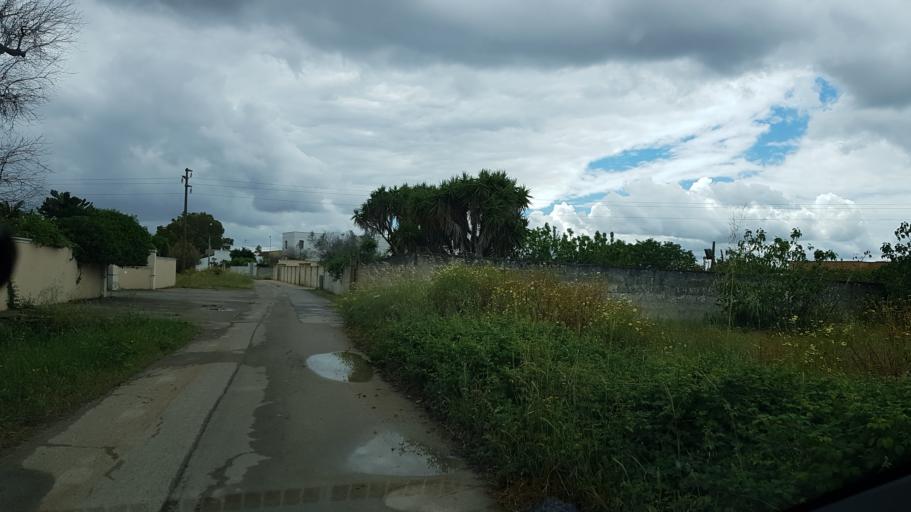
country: IT
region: Apulia
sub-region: Provincia di Brindisi
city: Torchiarolo
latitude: 40.4921
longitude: 18.0499
